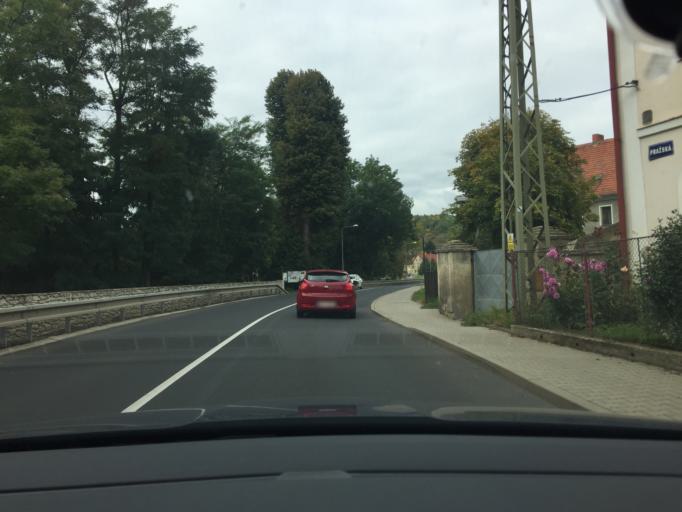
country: CZ
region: Ustecky
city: Kresice
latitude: 50.5208
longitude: 14.2175
